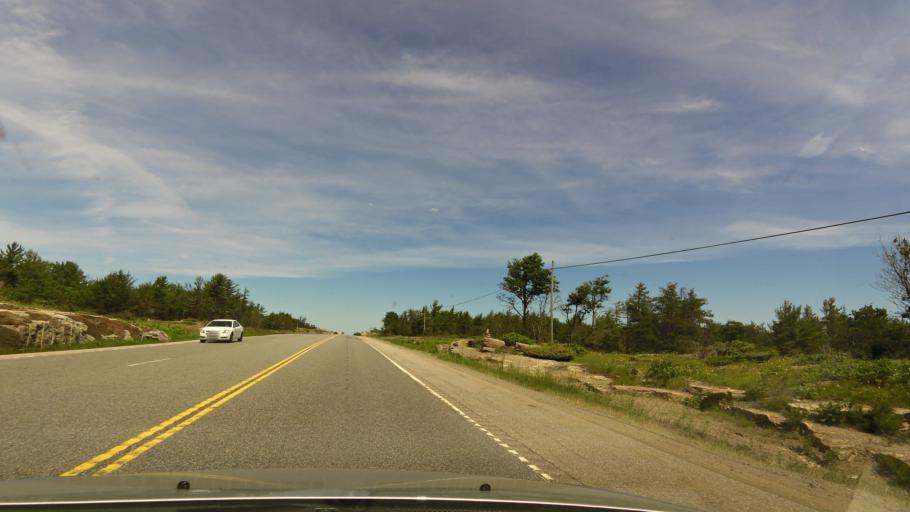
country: CA
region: Ontario
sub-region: Parry Sound District
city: Parry Sound
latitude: 45.4573
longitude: -80.1520
